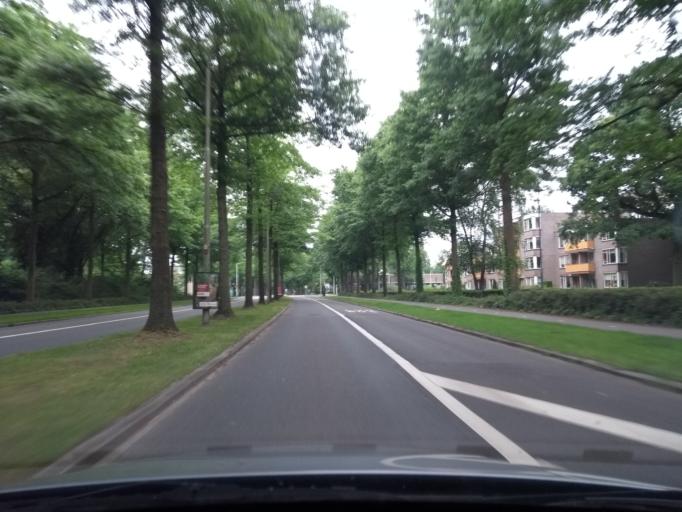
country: NL
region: Overijssel
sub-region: Gemeente Almelo
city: Almelo
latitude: 52.3712
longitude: 6.6784
